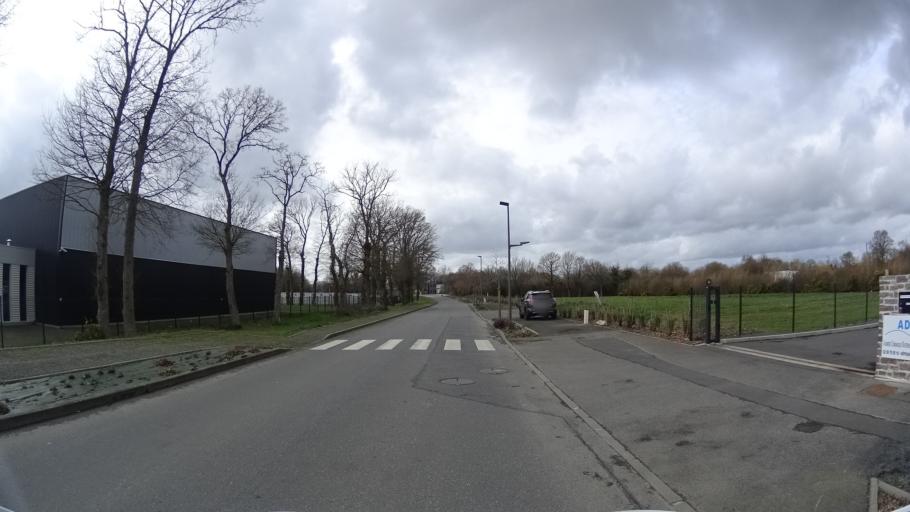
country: FR
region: Brittany
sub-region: Departement d'Ille-et-Vilaine
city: Saint-Gilles
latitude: 48.1579
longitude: -1.8244
